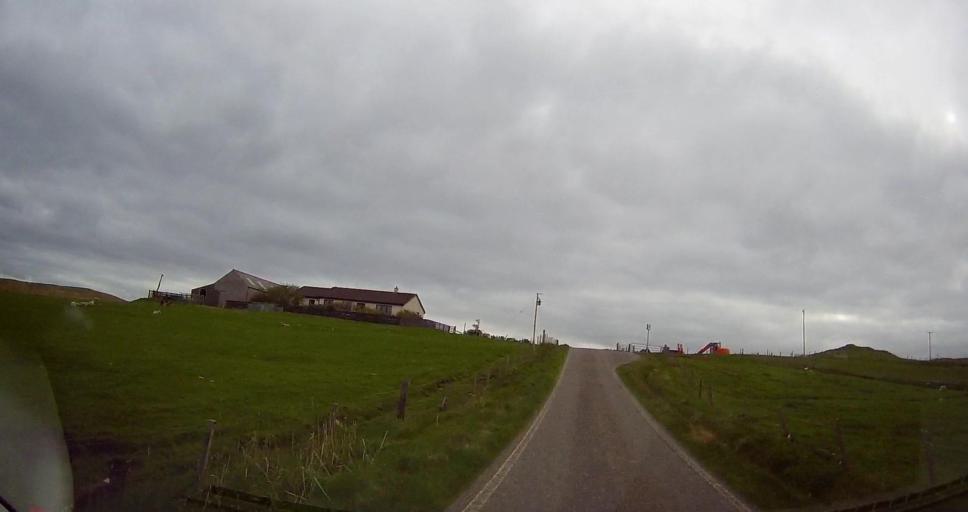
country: GB
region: Scotland
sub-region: Shetland Islands
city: Shetland
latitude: 60.4994
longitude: -1.0772
